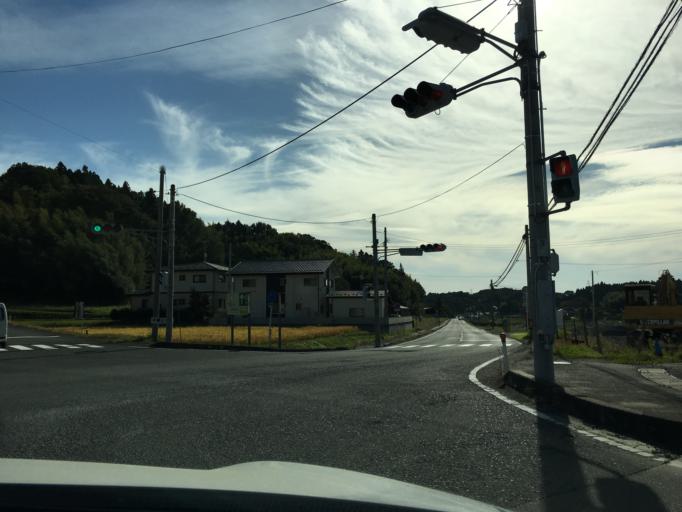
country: JP
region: Fukushima
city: Miharu
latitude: 37.4261
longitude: 140.4649
